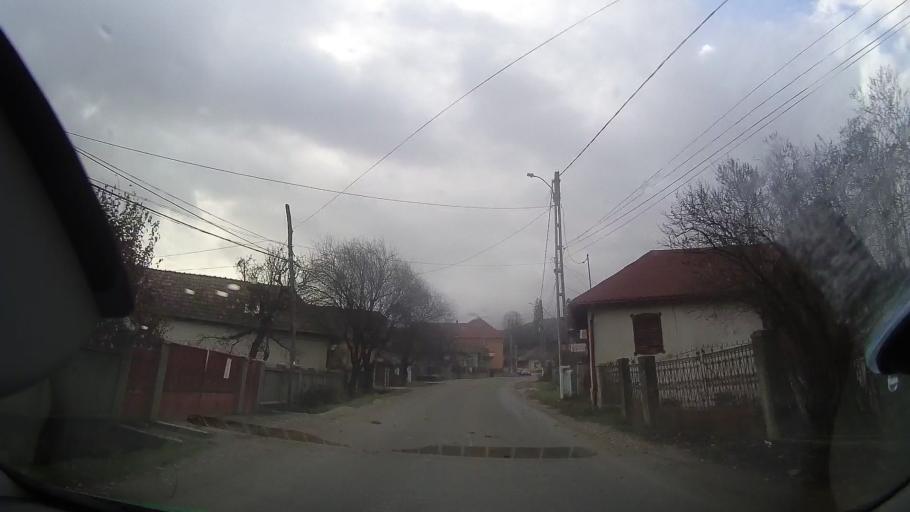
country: RO
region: Cluj
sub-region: Comuna Moldovenesti
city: Moldovenesti
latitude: 46.5021
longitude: 23.6647
